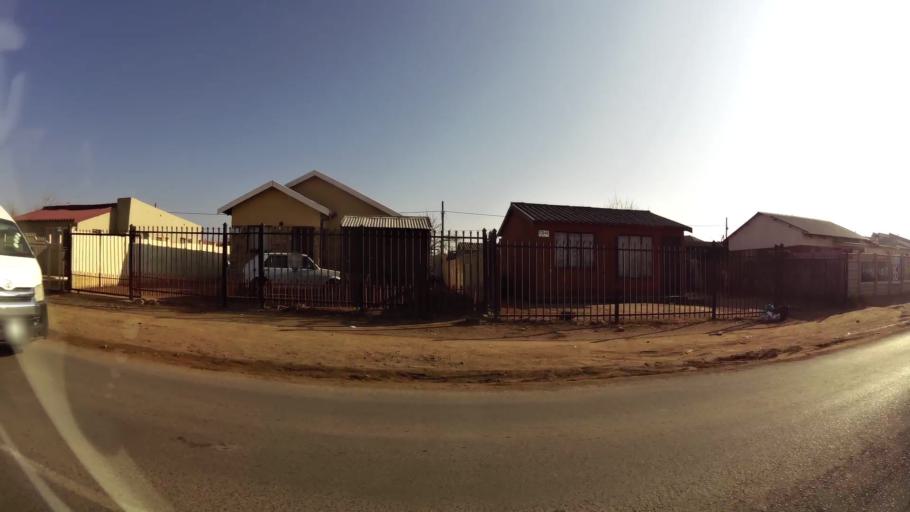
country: ZA
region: Orange Free State
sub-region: Mangaung Metropolitan Municipality
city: Bloemfontein
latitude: -29.1999
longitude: 26.2243
